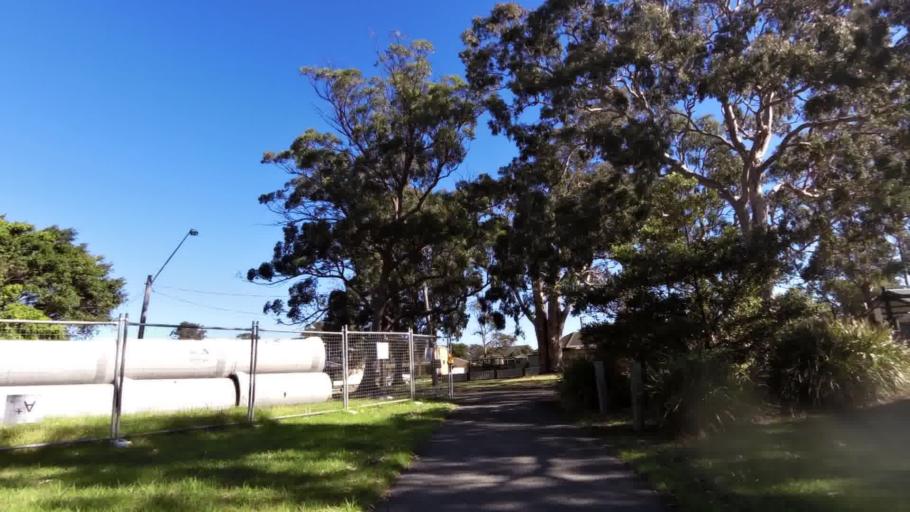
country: AU
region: New South Wales
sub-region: Shellharbour
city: Albion Park Rail
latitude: -34.5554
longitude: 150.8184
